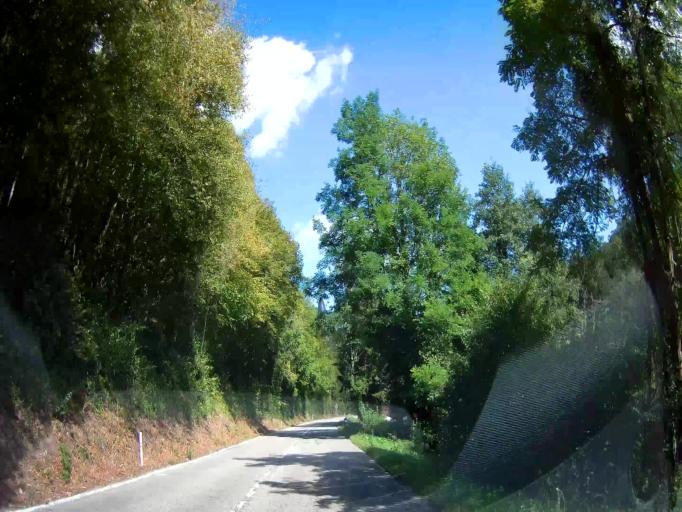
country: BE
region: Wallonia
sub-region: Province de Namur
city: Houyet
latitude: 50.2199
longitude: 4.9790
